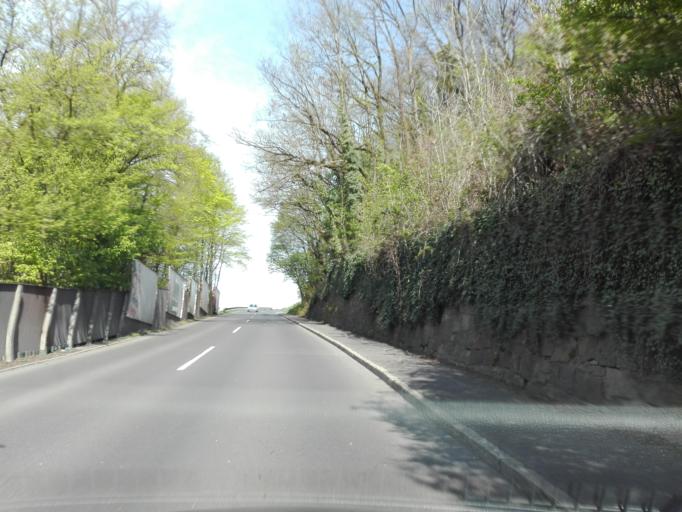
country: AT
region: Upper Austria
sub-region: Linz Stadt
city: Linz
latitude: 48.3179
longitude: 14.2541
